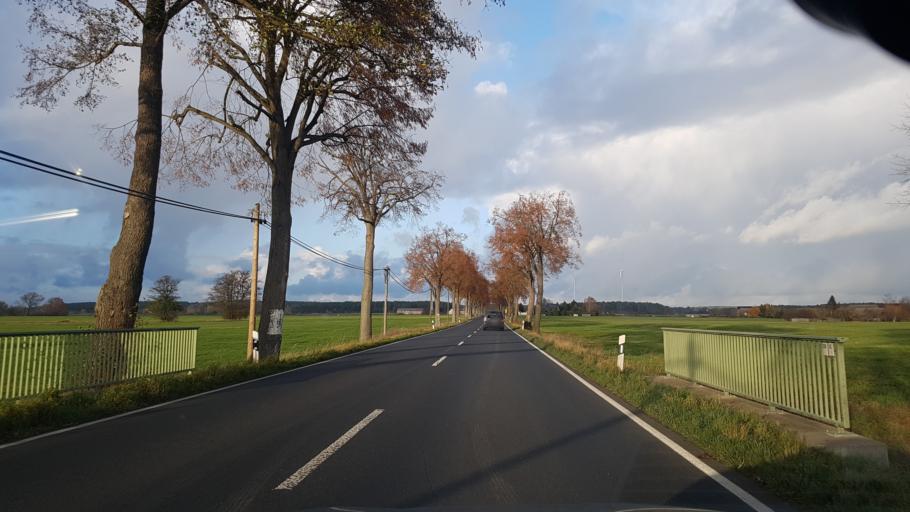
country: DE
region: Brandenburg
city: Sonnewalde
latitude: 51.7057
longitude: 13.6648
